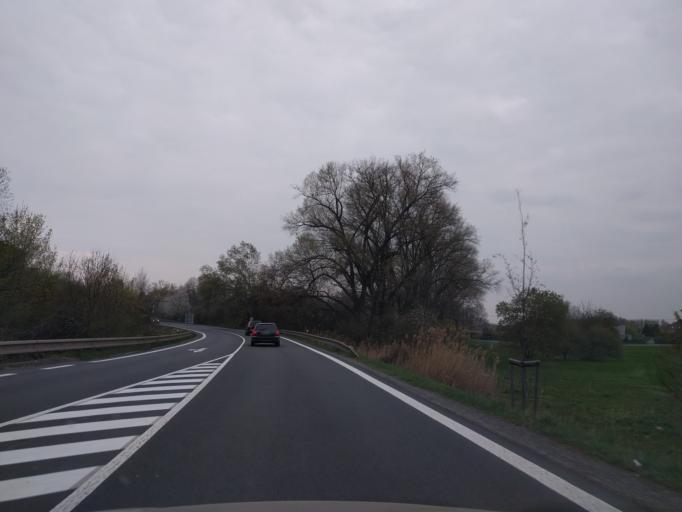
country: CZ
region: Central Bohemia
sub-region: Okres Praha-Vychod
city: Ricany
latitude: 49.9986
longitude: 14.6547
